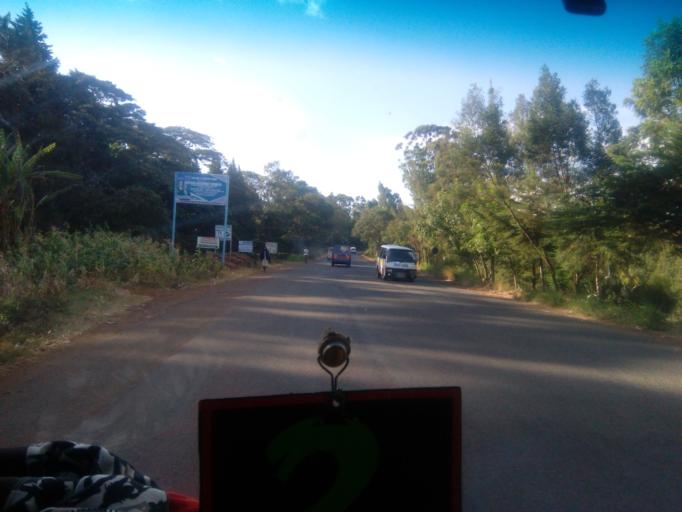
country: KE
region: Kiambu
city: Kikuyu
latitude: -1.2625
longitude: 36.6693
